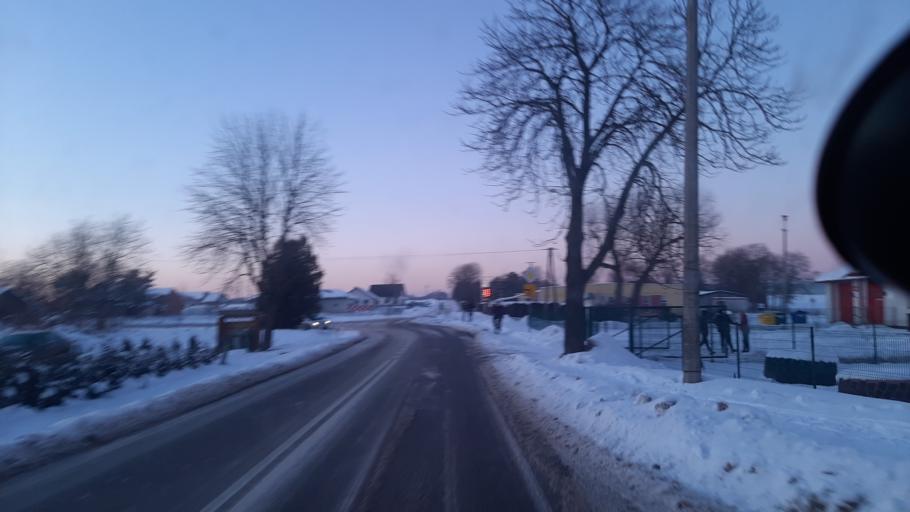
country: PL
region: Lublin Voivodeship
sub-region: Powiat lubelski
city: Niemce
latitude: 51.3621
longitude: 22.5300
